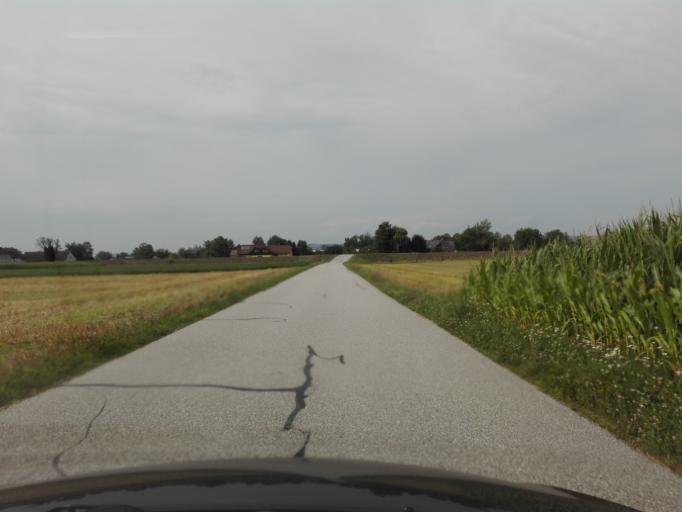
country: AT
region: Lower Austria
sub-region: Politischer Bezirk Amstetten
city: Strengberg
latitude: 48.1826
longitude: 14.6989
